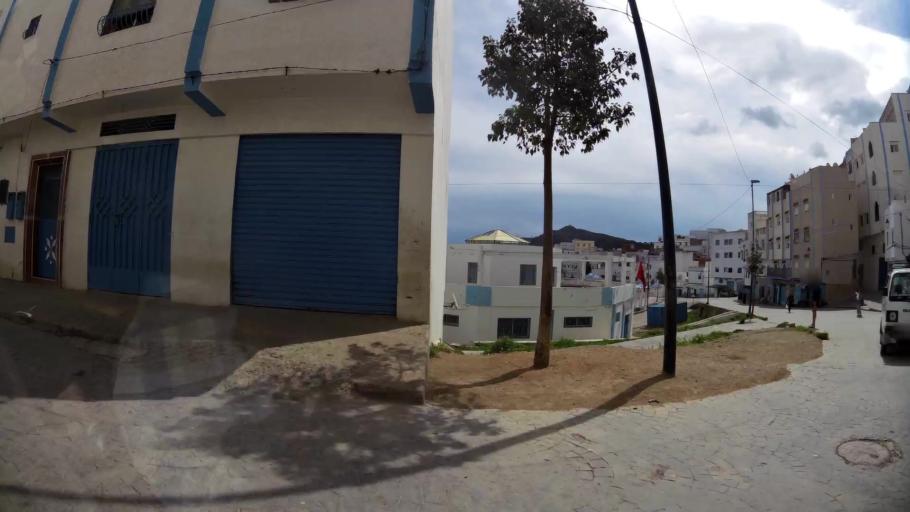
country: MA
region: Tanger-Tetouan
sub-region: Tetouan
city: Martil
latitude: 35.6835
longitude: -5.3333
